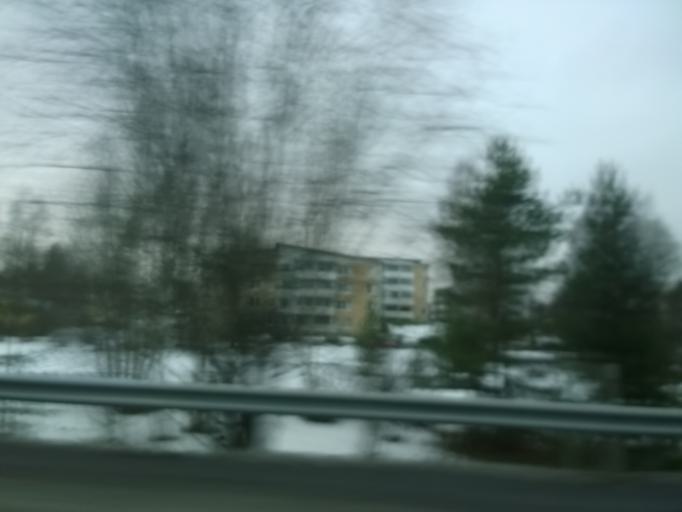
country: FI
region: Pirkanmaa
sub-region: Tampere
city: Lempaeaelae
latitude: 61.3088
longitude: 23.7589
